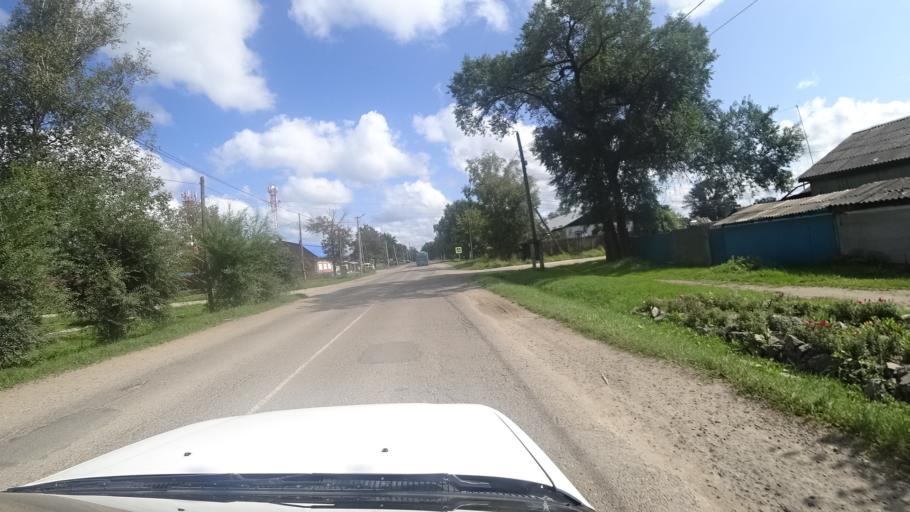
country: RU
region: Primorskiy
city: Dal'nerechensk
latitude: 45.9294
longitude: 133.7628
